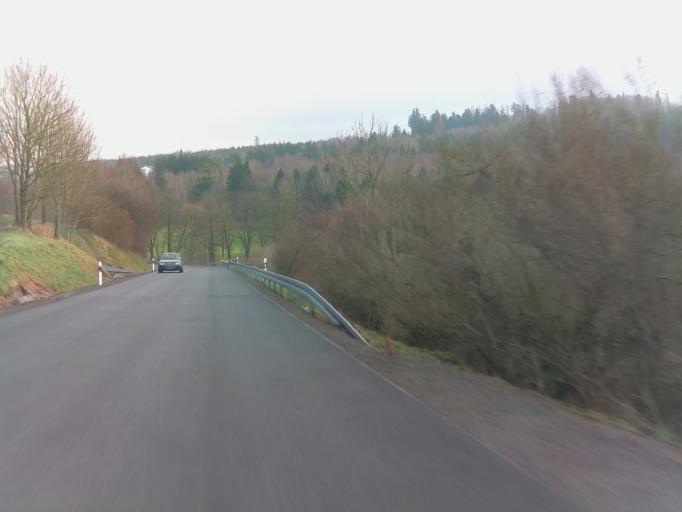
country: DE
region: Hesse
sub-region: Regierungsbezirk Kassel
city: Hilders
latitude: 50.5597
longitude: 9.9334
